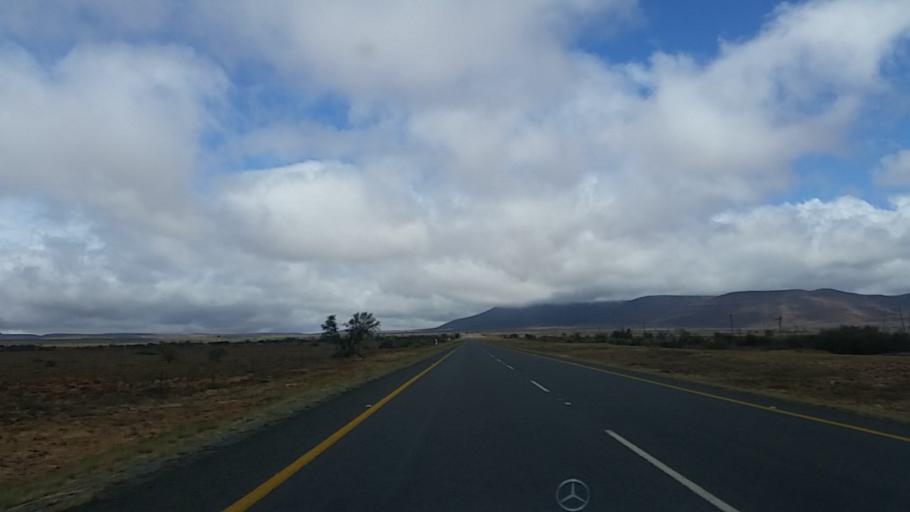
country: ZA
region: Eastern Cape
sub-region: Cacadu District Municipality
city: Graaff-Reinet
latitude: -32.0089
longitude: 24.6550
